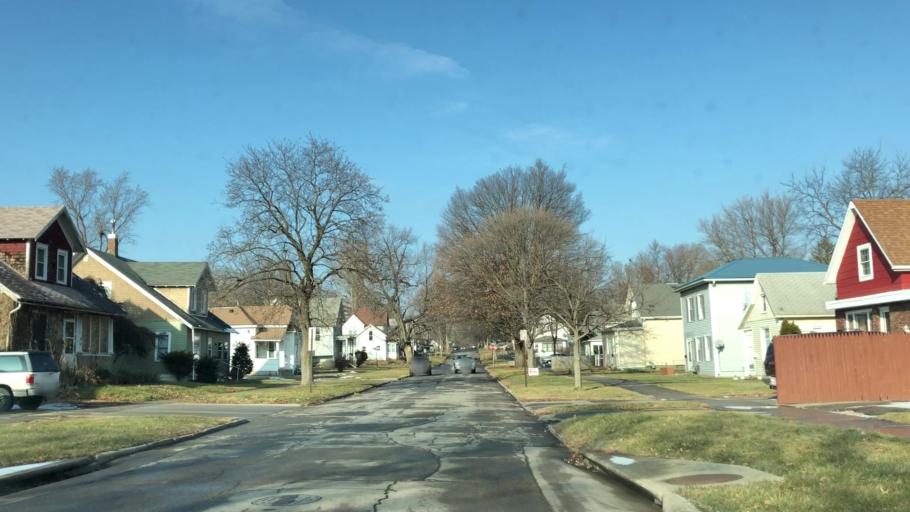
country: US
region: Iowa
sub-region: Marshall County
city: Marshalltown
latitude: 42.0455
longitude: -92.9193
